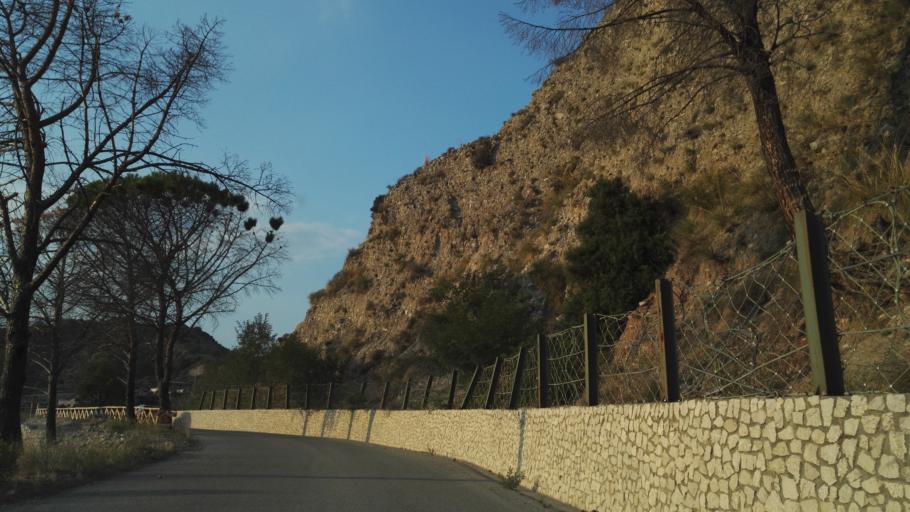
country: IT
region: Calabria
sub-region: Provincia di Reggio Calabria
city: Placanica
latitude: 38.4035
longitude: 16.4291
